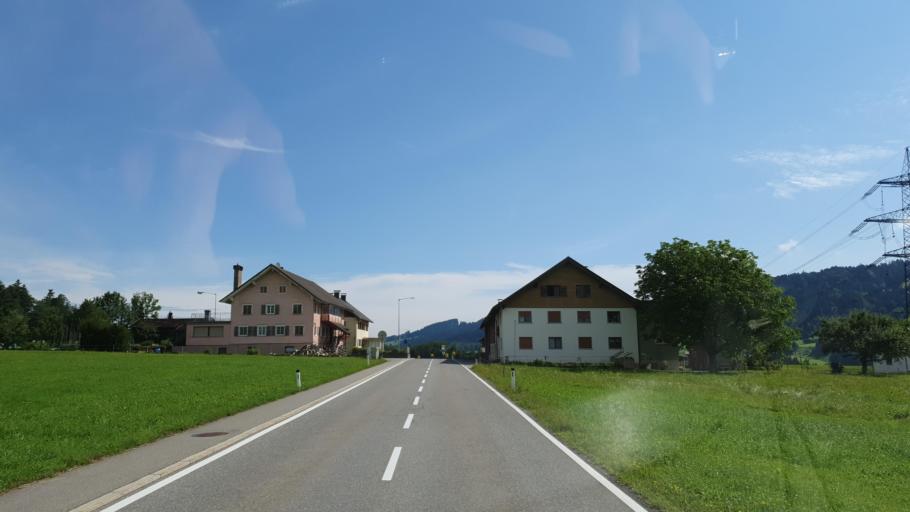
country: AT
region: Vorarlberg
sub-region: Politischer Bezirk Bregenz
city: Sulzberg
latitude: 47.5287
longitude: 9.8622
